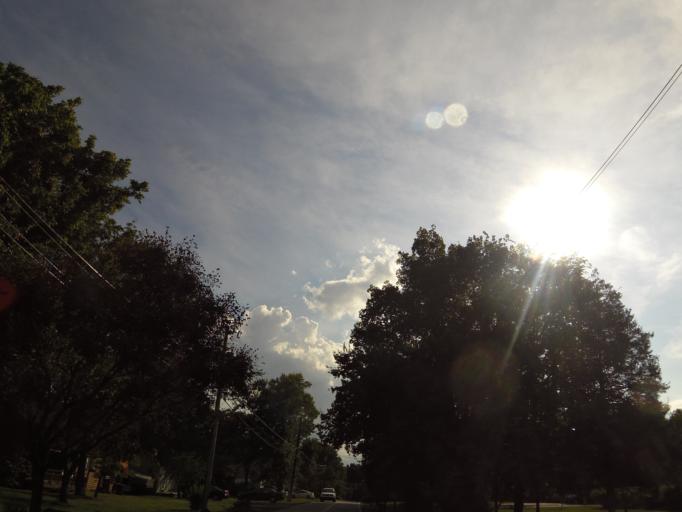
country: US
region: Tennessee
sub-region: Knox County
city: Knoxville
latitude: 36.0236
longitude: -83.9394
